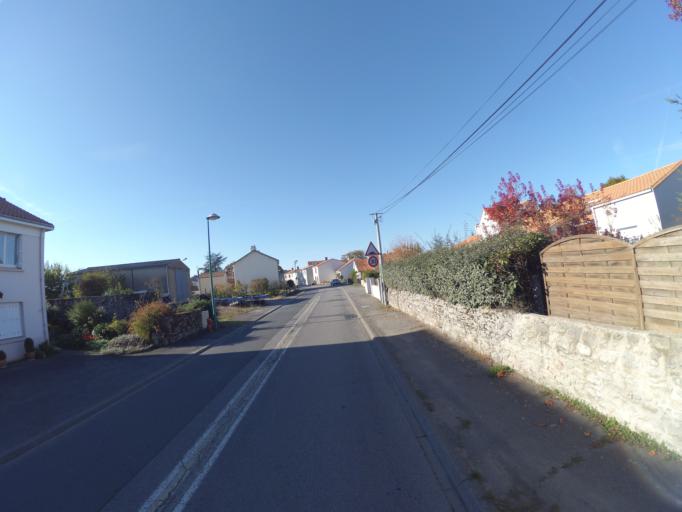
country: FR
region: Pays de la Loire
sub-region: Departement de la Loire-Atlantique
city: Saint-Lumine-de-Clisson
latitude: 47.0822
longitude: -1.3340
